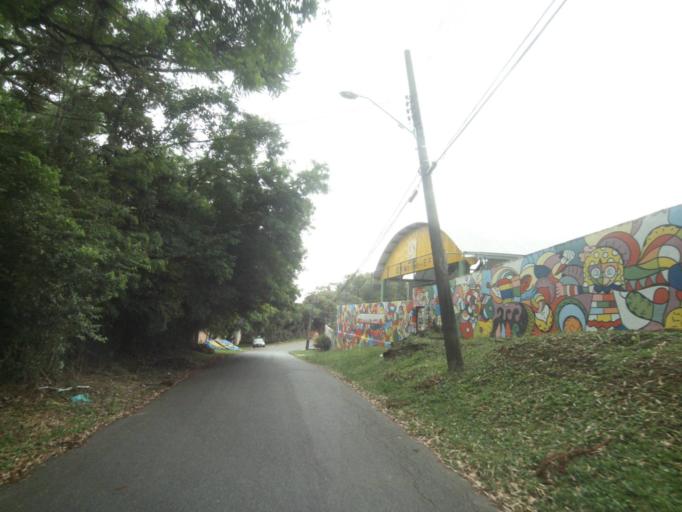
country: BR
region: Parana
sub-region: Curitiba
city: Curitiba
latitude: -25.3997
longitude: -49.2972
